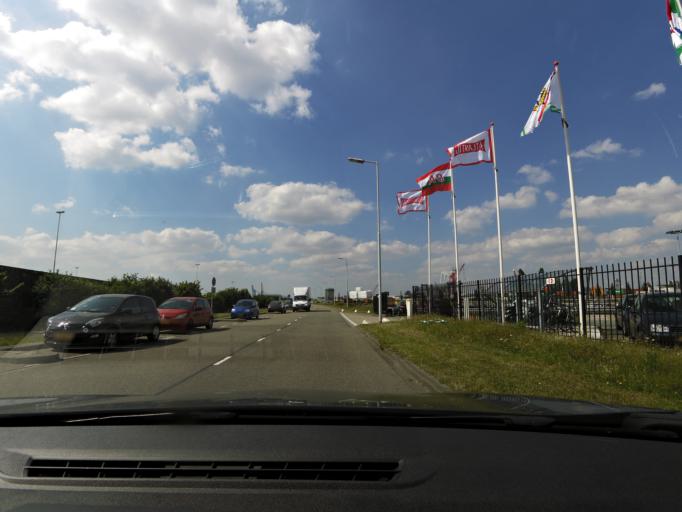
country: NL
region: South Holland
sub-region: Gemeente Schiedam
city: Schiedam
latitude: 51.8933
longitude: 4.3782
